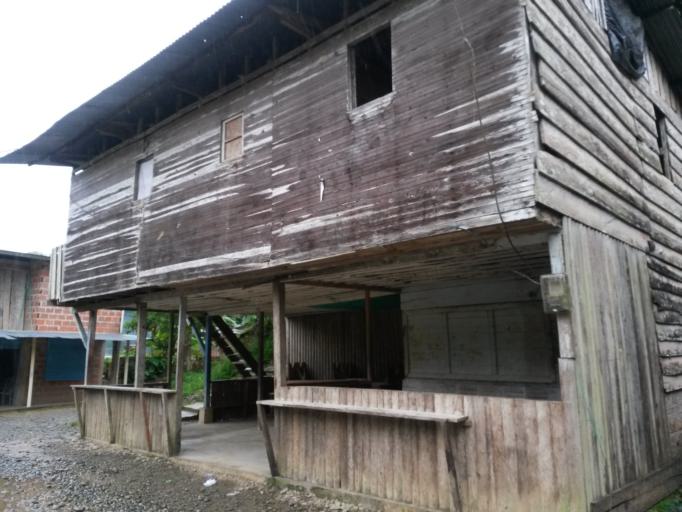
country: CO
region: Valle del Cauca
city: Buenaventura
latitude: 3.8412
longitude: -76.8992
